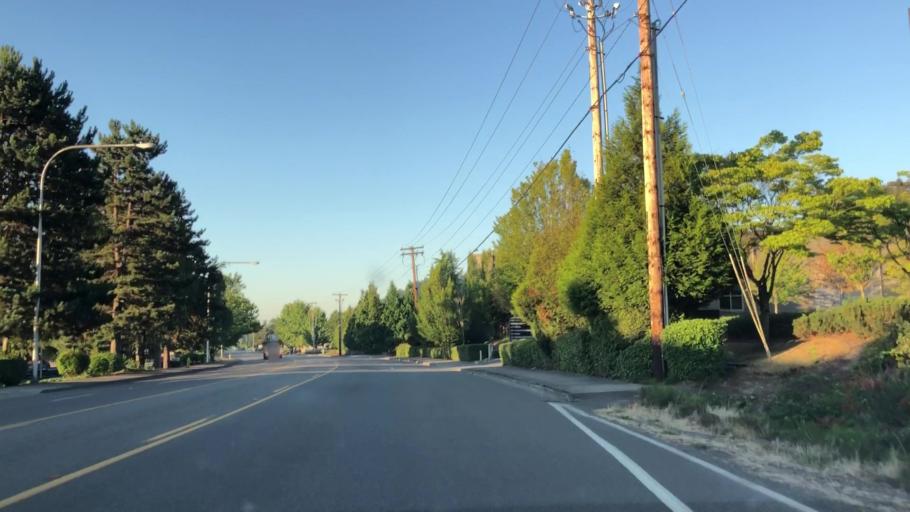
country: US
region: Washington
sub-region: King County
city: Lakeland North
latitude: 47.3325
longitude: -122.2497
